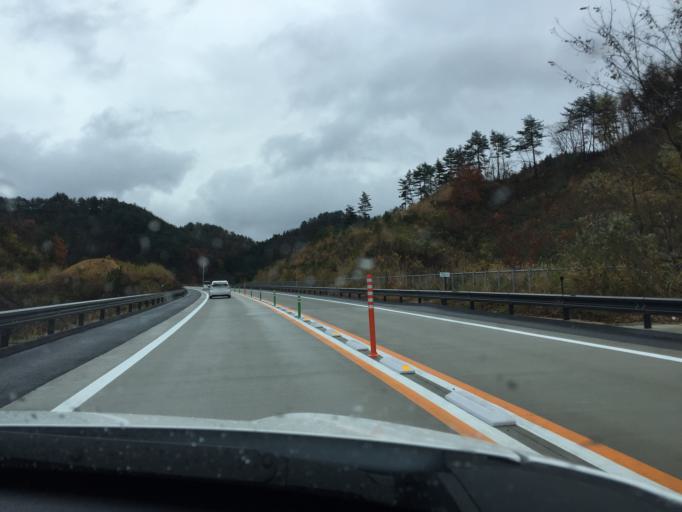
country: JP
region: Yamagata
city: Yonezawa
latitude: 37.8767
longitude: 140.1882
